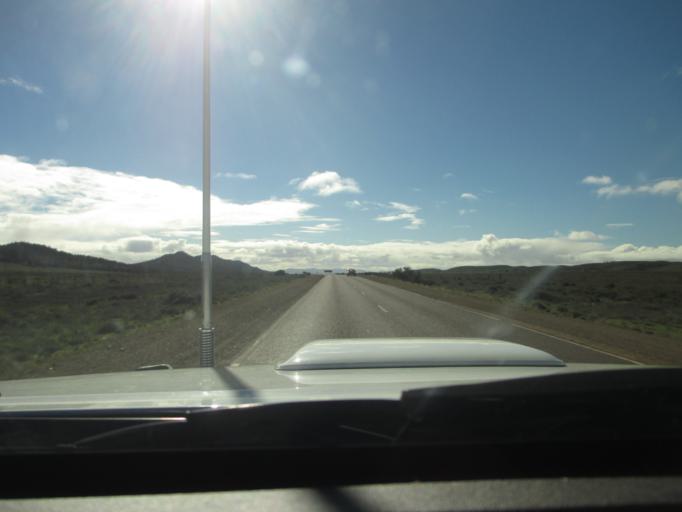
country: AU
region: South Australia
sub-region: Flinders Ranges
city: Quorn
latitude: -31.9518
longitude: 138.3943
